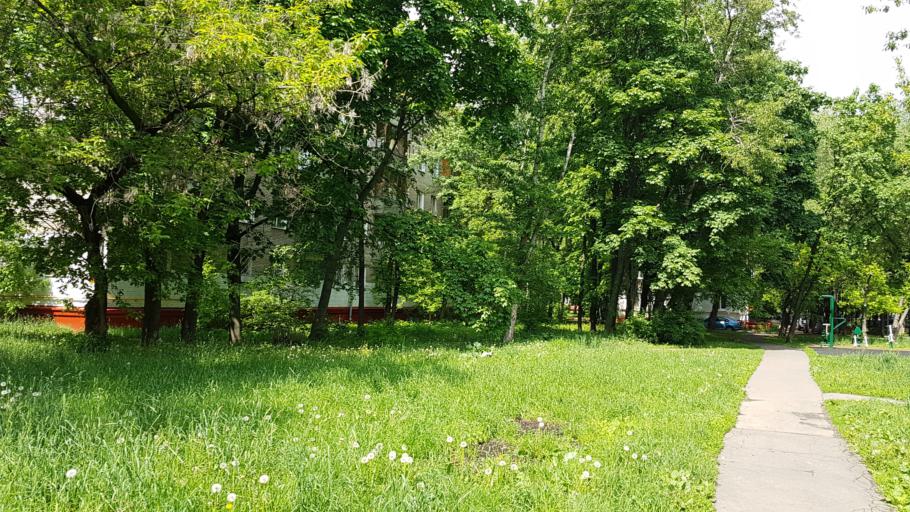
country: RU
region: Moskovskaya
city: Novogireyevo
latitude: 55.7519
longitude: 37.8256
